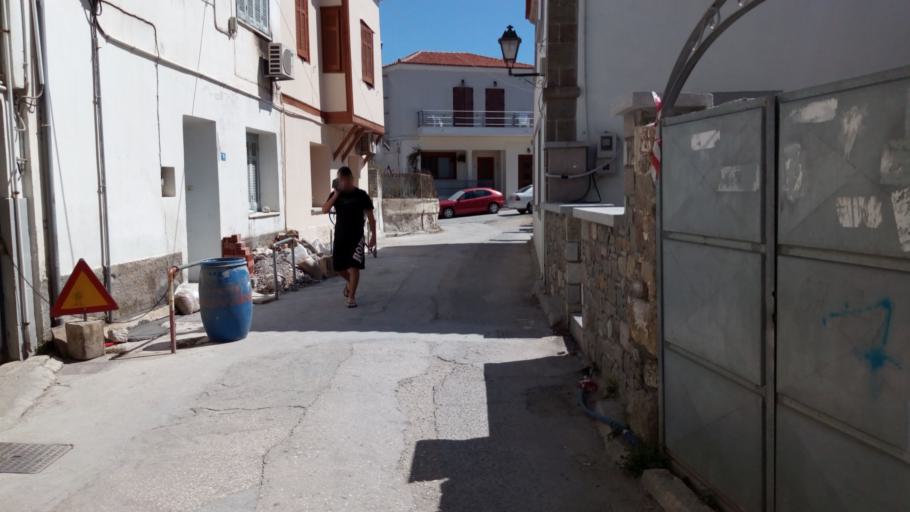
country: GR
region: North Aegean
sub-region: Nomos Lesvou
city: Myrina
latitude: 39.8764
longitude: 25.0606
